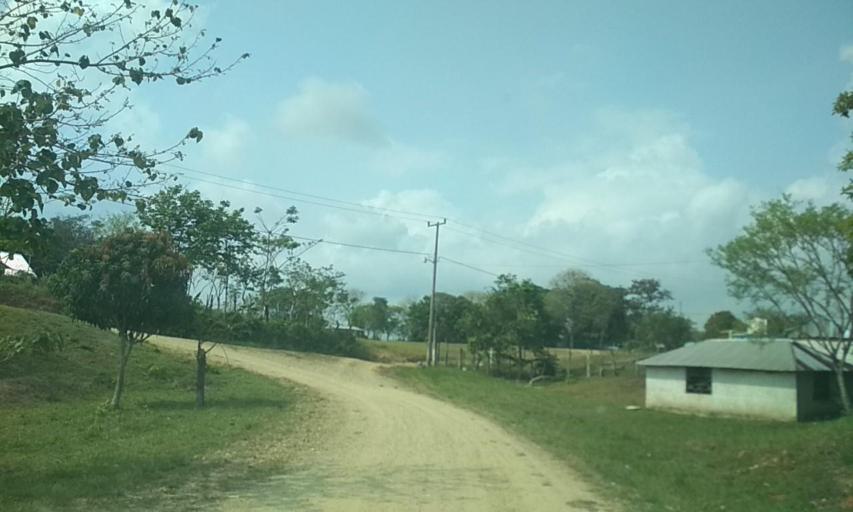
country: MX
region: Tabasco
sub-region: Huimanguillo
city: Francisco Rueda
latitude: 17.6555
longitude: -93.7541
